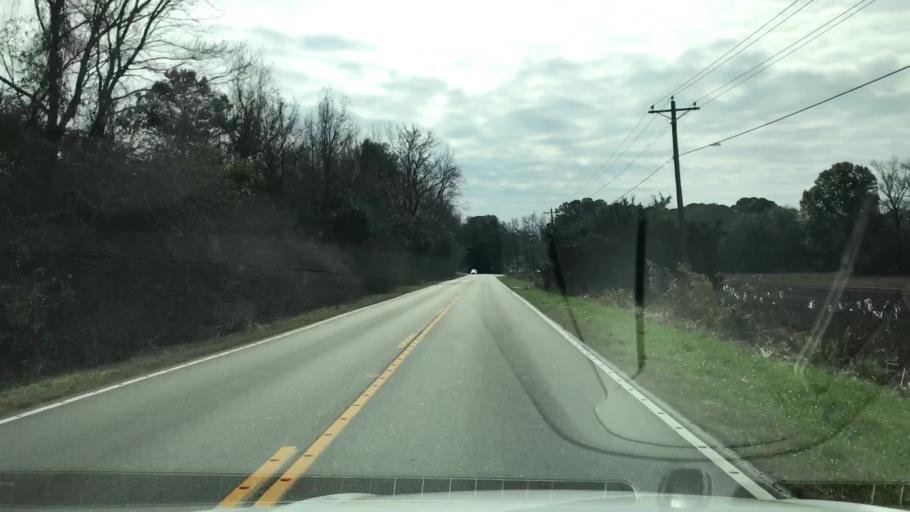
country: US
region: South Carolina
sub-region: Charleston County
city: Folly Beach
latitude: 32.7210
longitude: -80.0223
